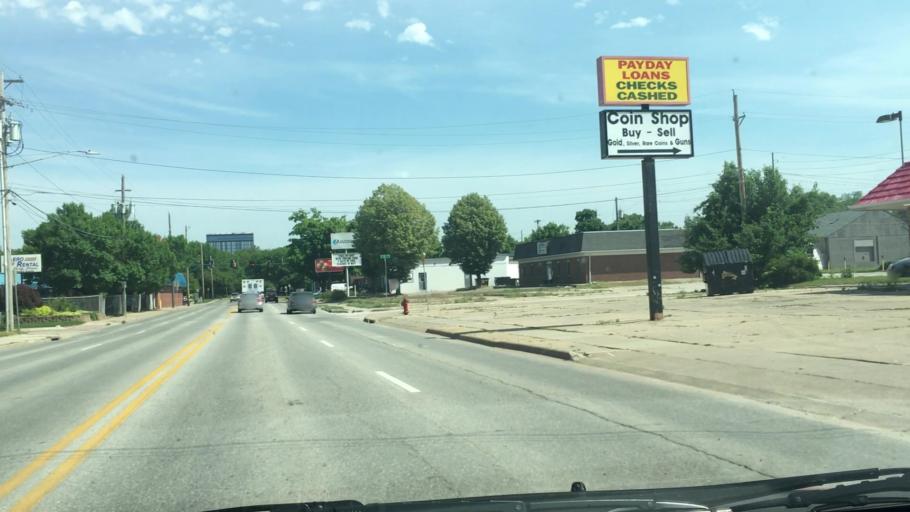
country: US
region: Iowa
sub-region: Johnson County
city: Iowa City
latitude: 41.6480
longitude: -91.5320
